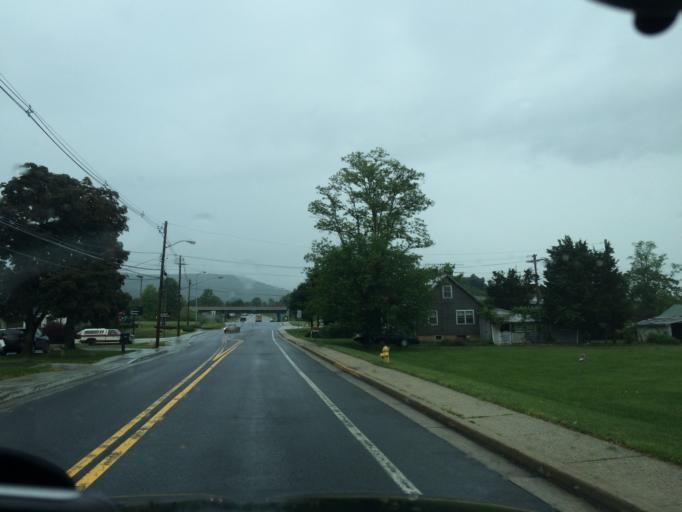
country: US
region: Maryland
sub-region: Frederick County
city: Thurmont
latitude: 39.6323
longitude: -77.4107
